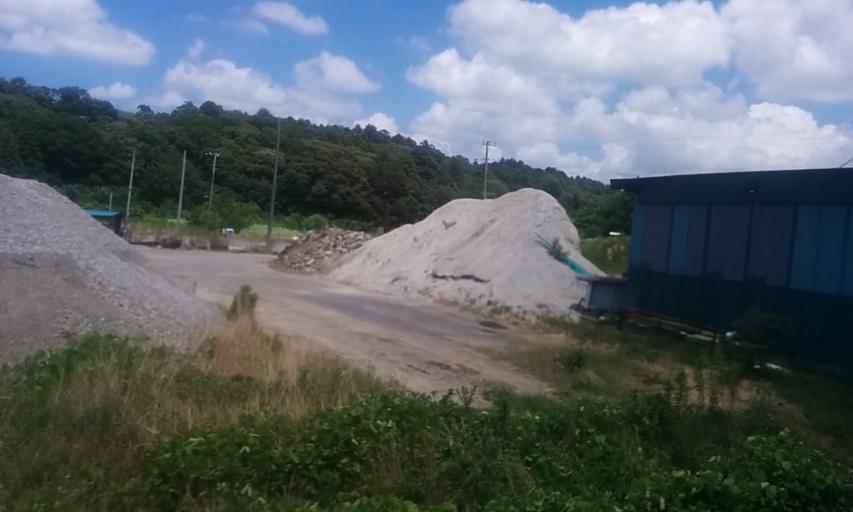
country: JP
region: Chiba
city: Chiba
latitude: 35.5679
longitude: 140.1494
